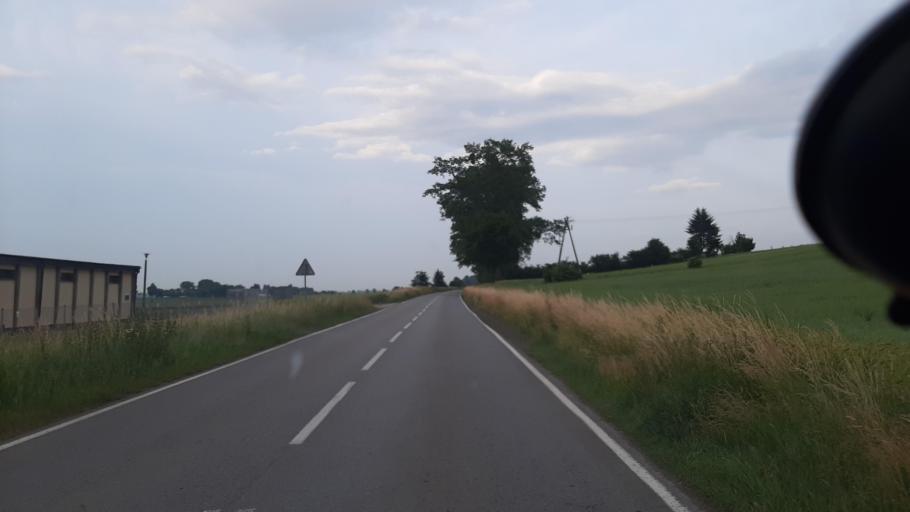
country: PL
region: Lublin Voivodeship
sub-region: Powiat lubelski
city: Garbow
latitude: 51.3477
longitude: 22.3728
